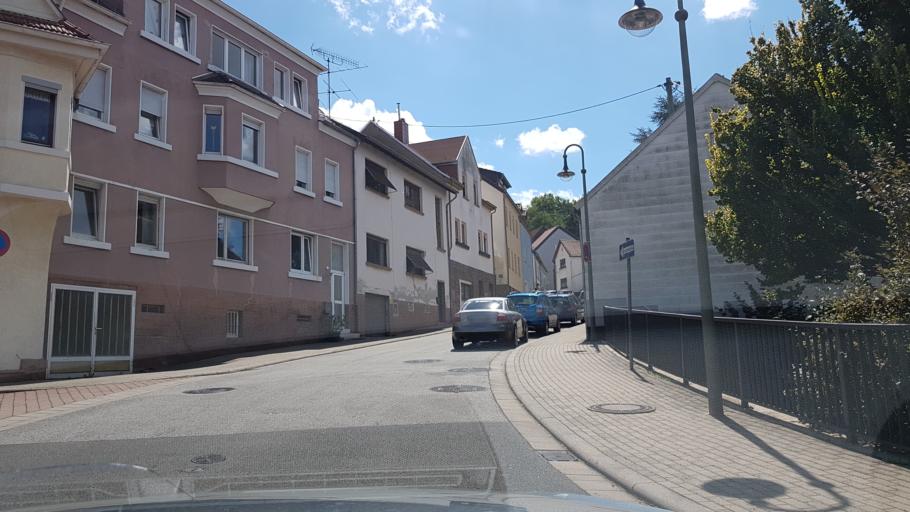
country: DE
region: Saarland
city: Illingen
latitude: 49.3721
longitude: 7.0824
